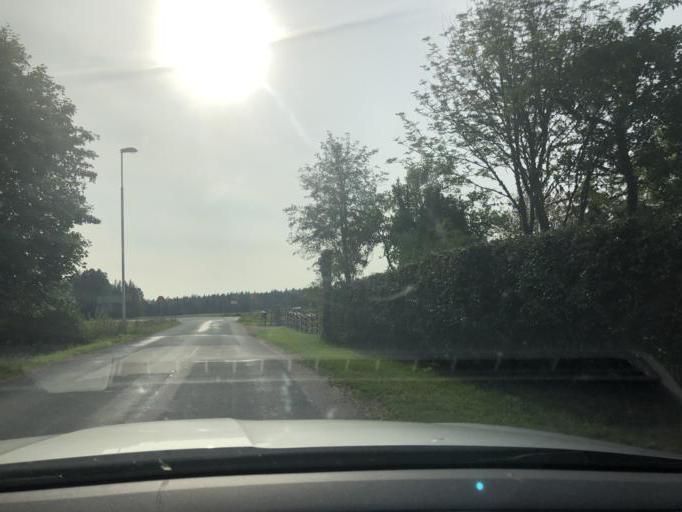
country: SE
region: Joenkoeping
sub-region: Vetlanda Kommun
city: Ekenassjon
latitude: 57.5098
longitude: 14.9047
